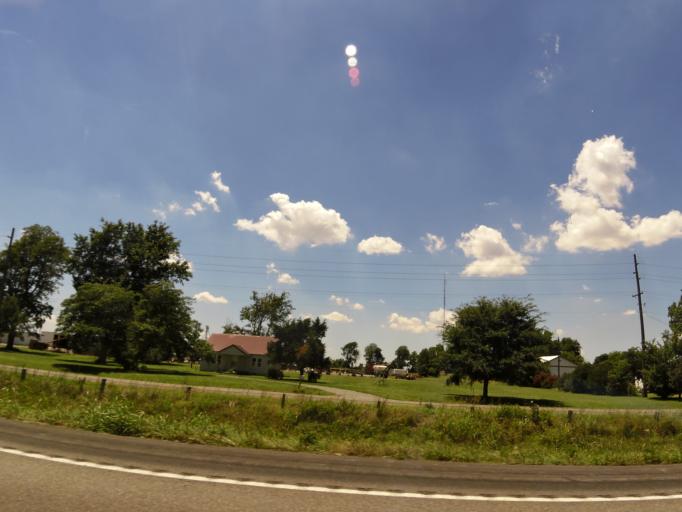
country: US
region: Missouri
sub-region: New Madrid County
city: Portageville
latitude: 36.3366
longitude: -89.7014
